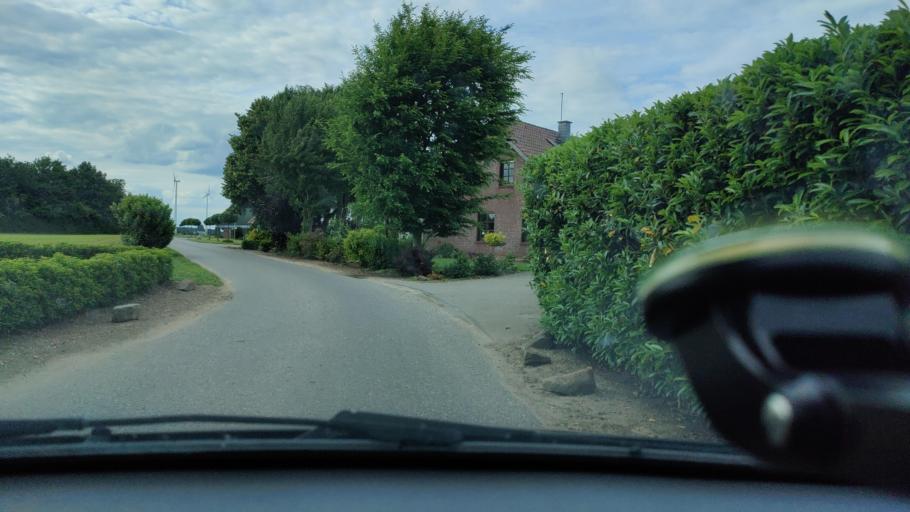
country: DE
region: North Rhine-Westphalia
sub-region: Regierungsbezirk Dusseldorf
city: Weeze
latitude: 51.6554
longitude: 6.1924
